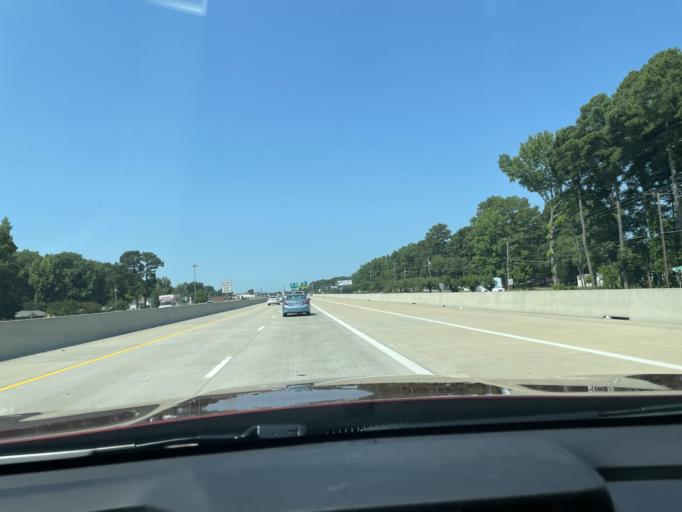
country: US
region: Arkansas
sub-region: Pulaski County
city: Jacksonville
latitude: 34.8950
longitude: -92.0954
